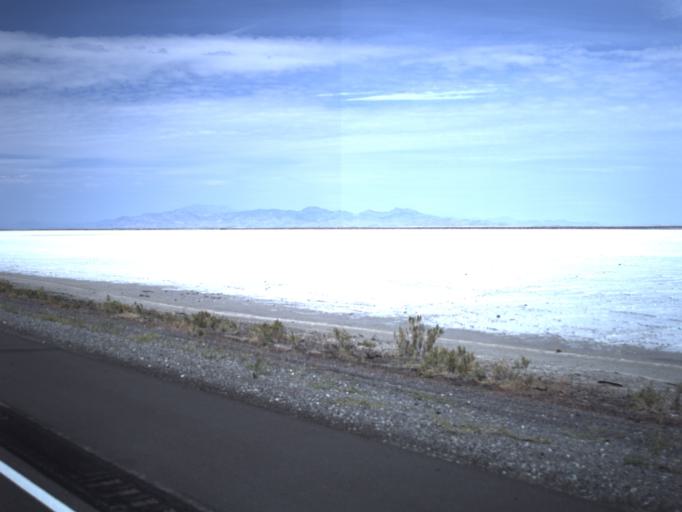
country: US
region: Utah
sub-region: Tooele County
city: Wendover
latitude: 40.7294
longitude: -113.3978
